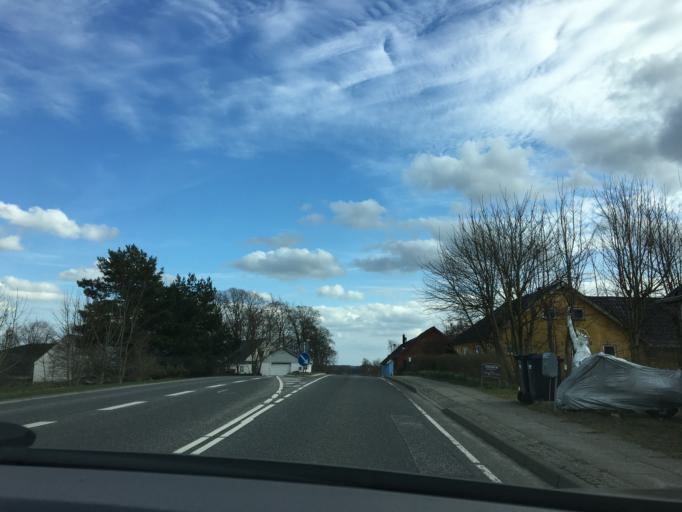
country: DK
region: South Denmark
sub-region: Vejle Kommune
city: Give
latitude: 55.8298
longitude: 9.3174
